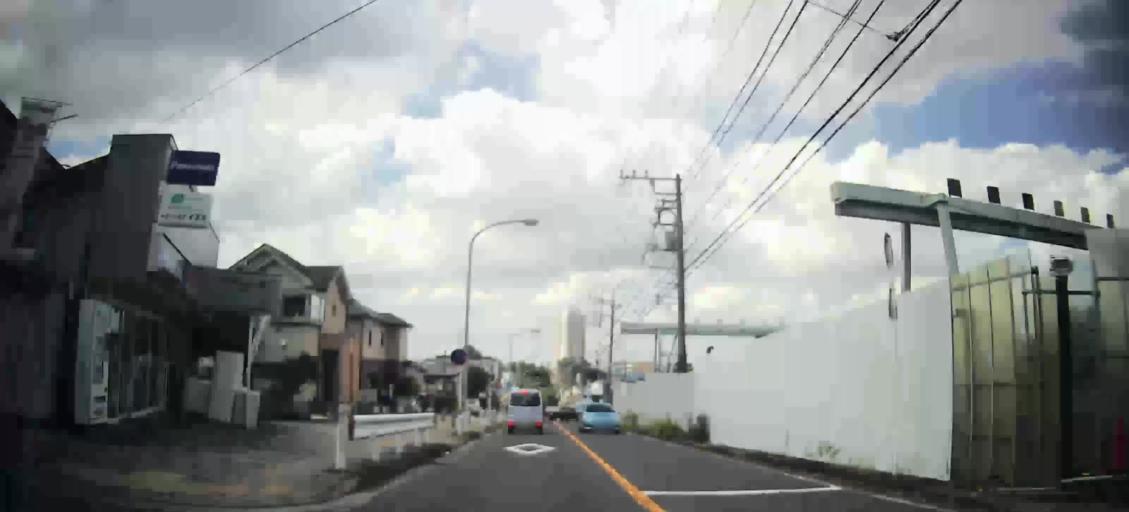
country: JP
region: Kanagawa
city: Yokohama
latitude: 35.4698
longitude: 139.5567
